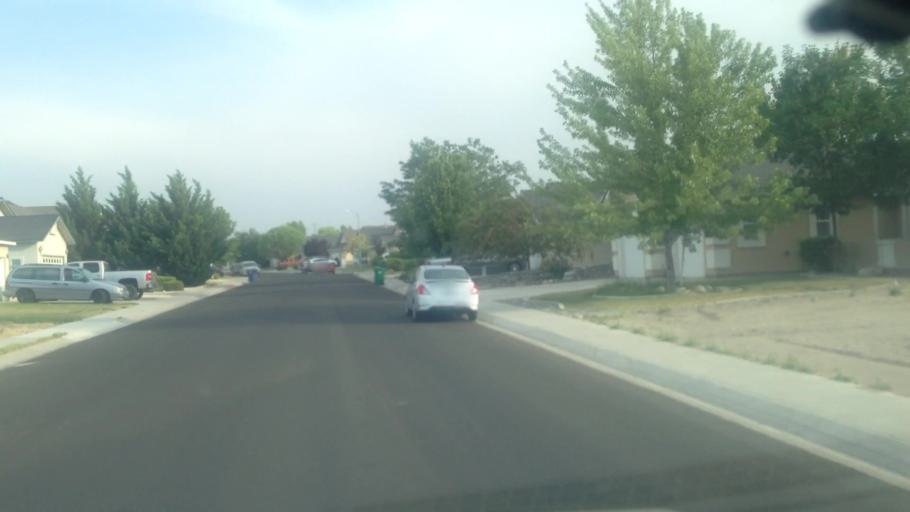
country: US
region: Nevada
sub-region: Lyon County
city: Fernley
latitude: 39.5911
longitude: -119.1546
